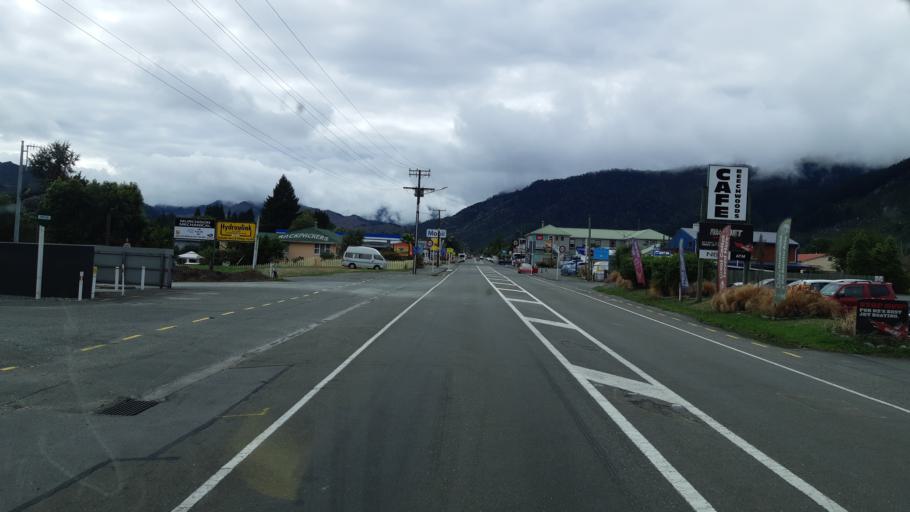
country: NZ
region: West Coast
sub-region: Buller District
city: Westport
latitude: -41.8001
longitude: 172.3227
